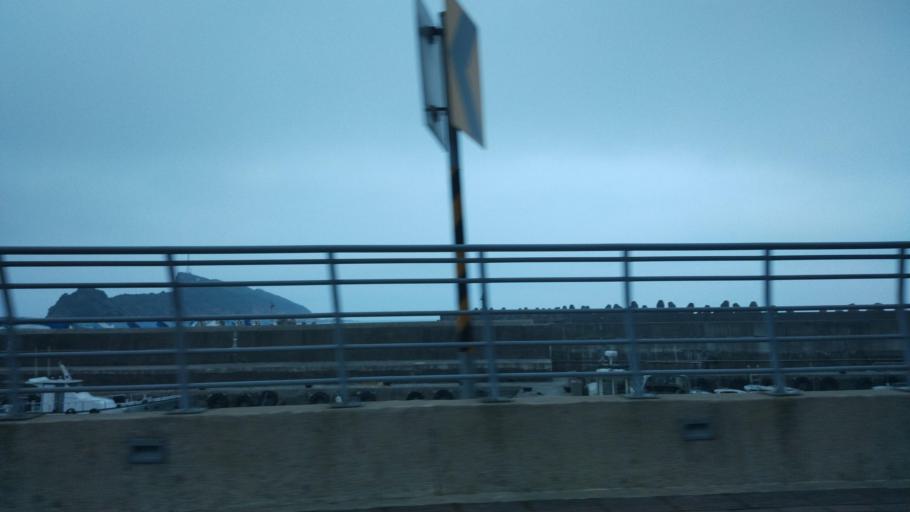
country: TW
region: Taiwan
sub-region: Keelung
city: Keelung
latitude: 25.2031
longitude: 121.6925
